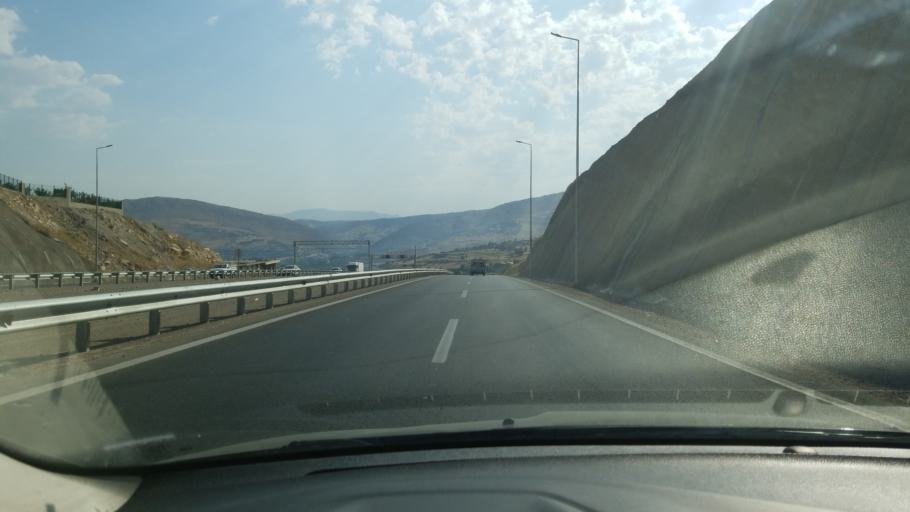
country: IQ
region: Arbil
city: Shaqlawah
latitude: 36.3821
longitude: 44.2280
